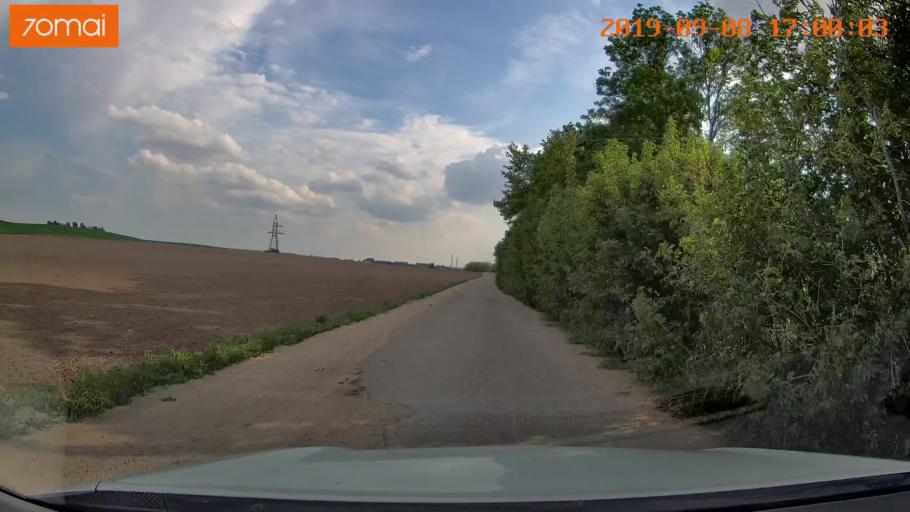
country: BY
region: Grodnenskaya
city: Hrodna
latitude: 53.7184
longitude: 23.9328
